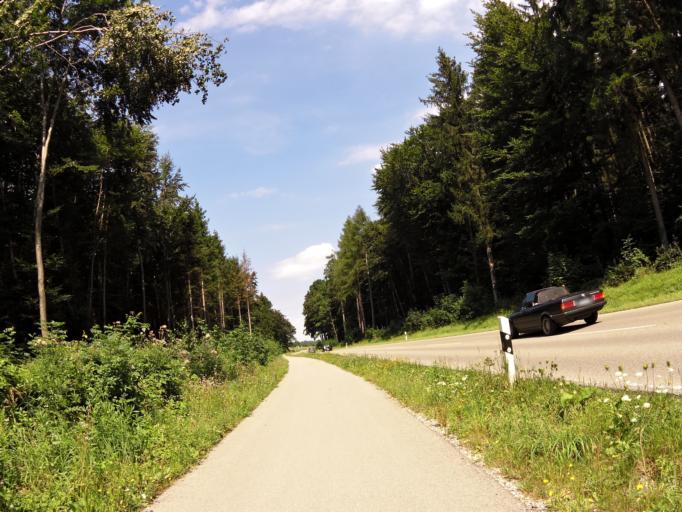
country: DE
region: Bavaria
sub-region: Upper Bavaria
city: Inning am Ammersee
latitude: 48.0596
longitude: 11.1430
